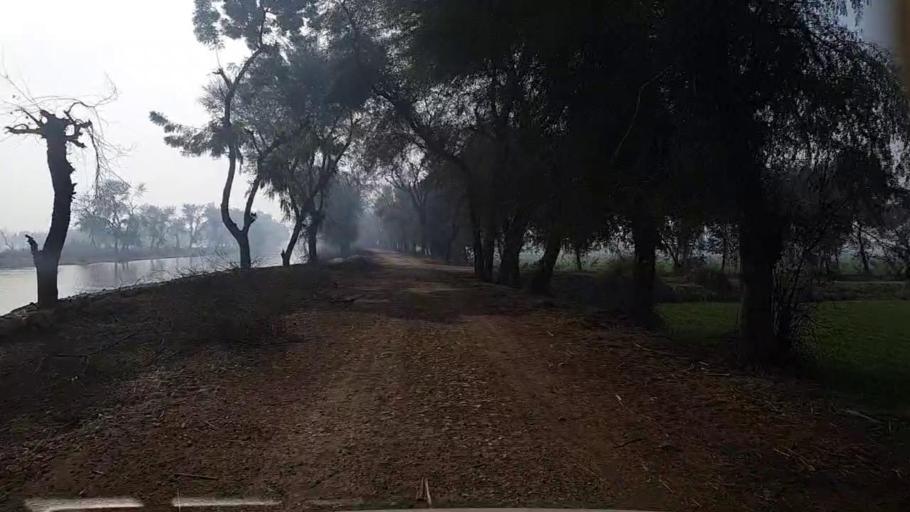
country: PK
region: Sindh
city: Khairpur
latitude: 27.9503
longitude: 69.6522
